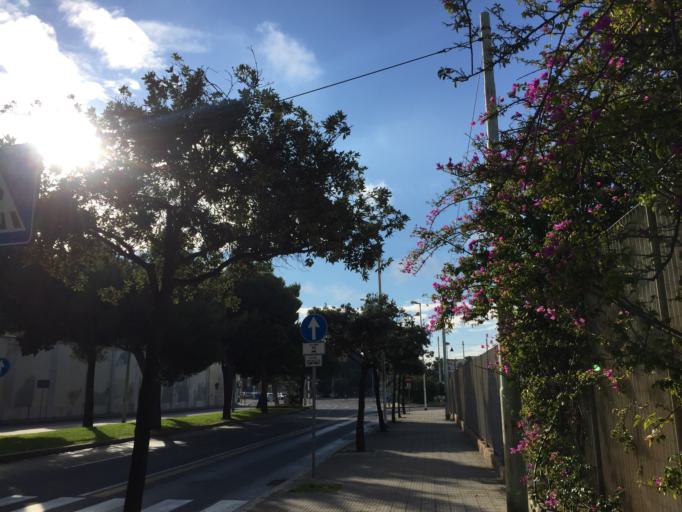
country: IT
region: Sardinia
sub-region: Provincia di Cagliari
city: Cagliari
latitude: 39.2108
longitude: 9.1229
